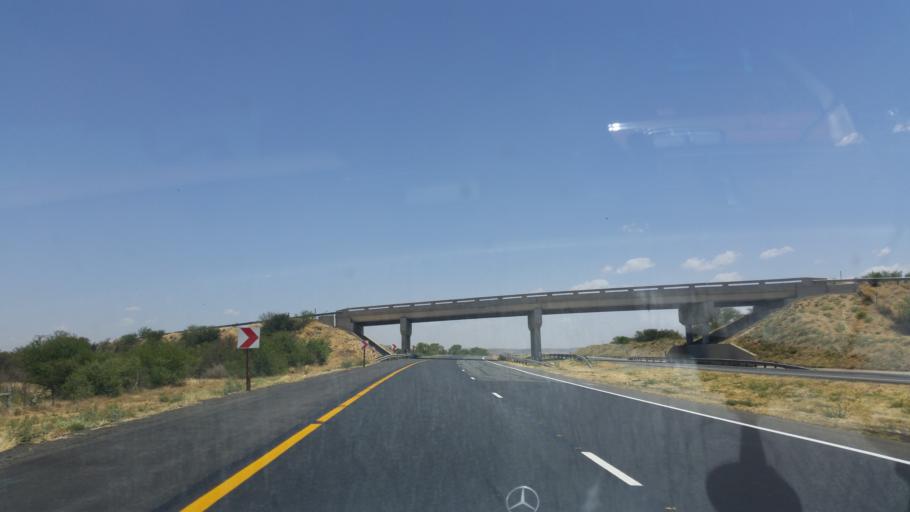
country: ZA
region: Orange Free State
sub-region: Mangaung Metropolitan Municipality
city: Bloemfontein
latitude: -28.9520
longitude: 26.3935
